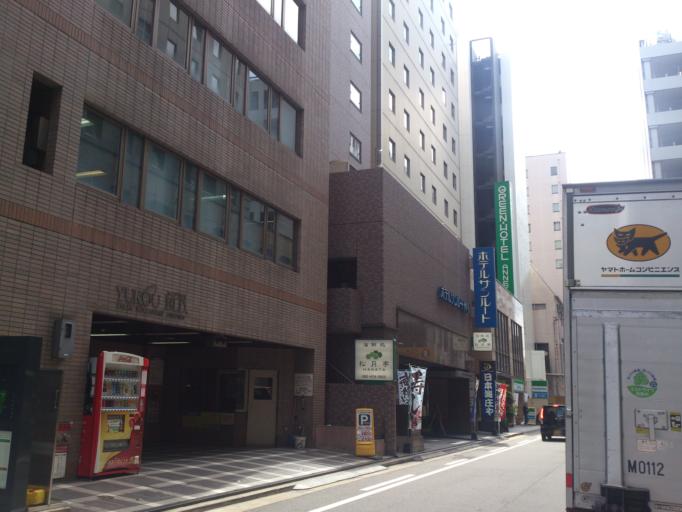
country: JP
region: Fukuoka
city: Fukuoka-shi
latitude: 33.5920
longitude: 130.4218
